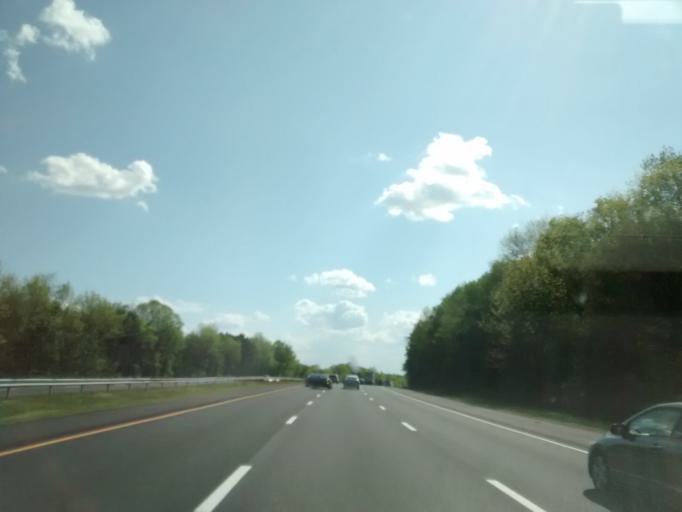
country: US
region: Connecticut
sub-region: Tolland County
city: Stafford
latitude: 41.9486
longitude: -72.2049
